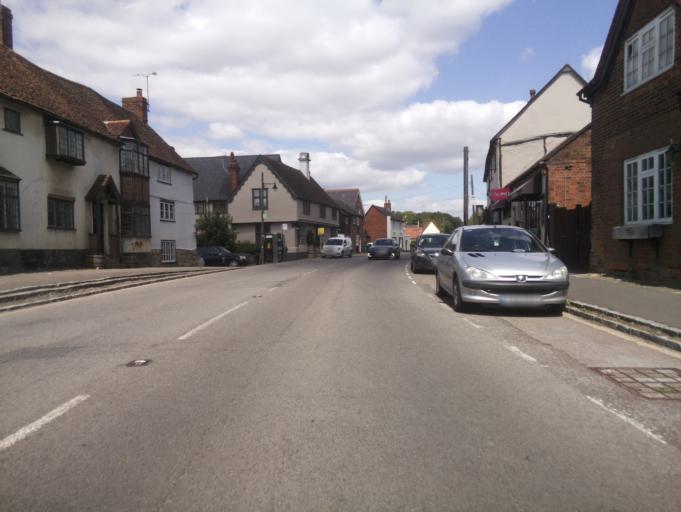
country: GB
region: England
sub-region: Buckinghamshire
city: Aylesbury
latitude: 51.8793
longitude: -0.8359
